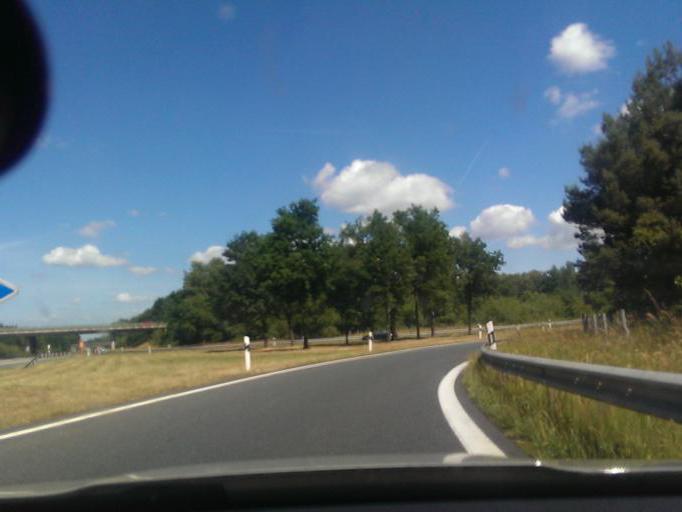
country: DE
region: Lower Saxony
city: Verden
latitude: 52.9581
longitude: 9.2467
